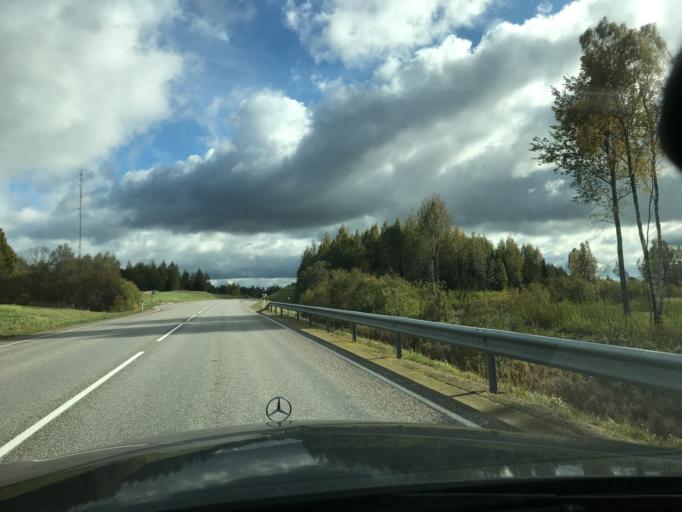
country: EE
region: Vorumaa
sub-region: Voru linn
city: Voru
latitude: 57.7495
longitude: 27.2379
